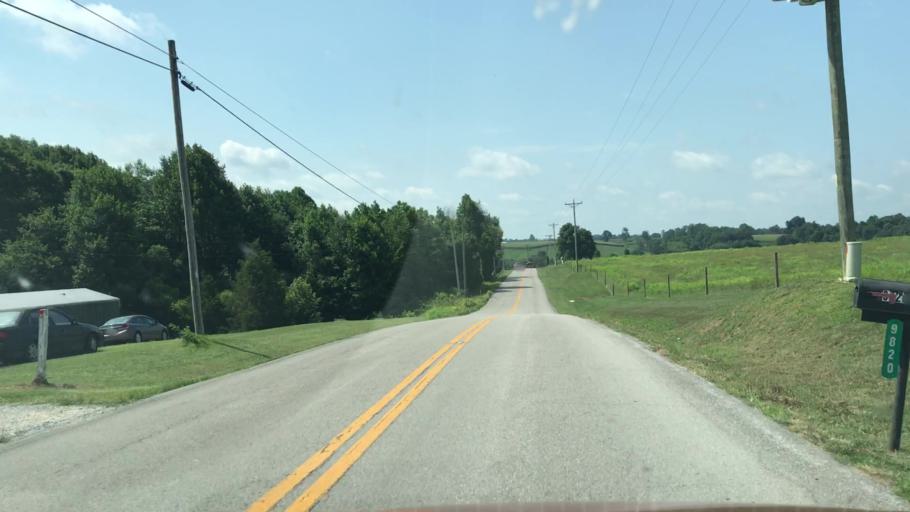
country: US
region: Kentucky
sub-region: Barren County
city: Glasgow
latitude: 36.8726
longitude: -85.8486
